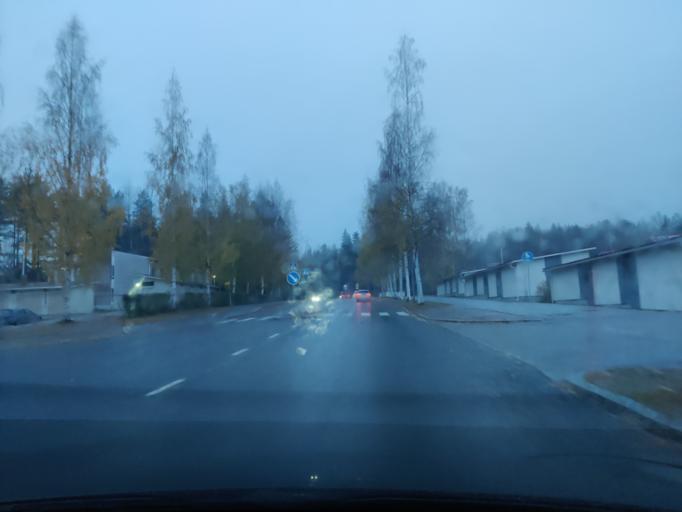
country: FI
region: Northern Savo
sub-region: Kuopio
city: Kuopio
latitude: 62.8412
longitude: 27.6572
